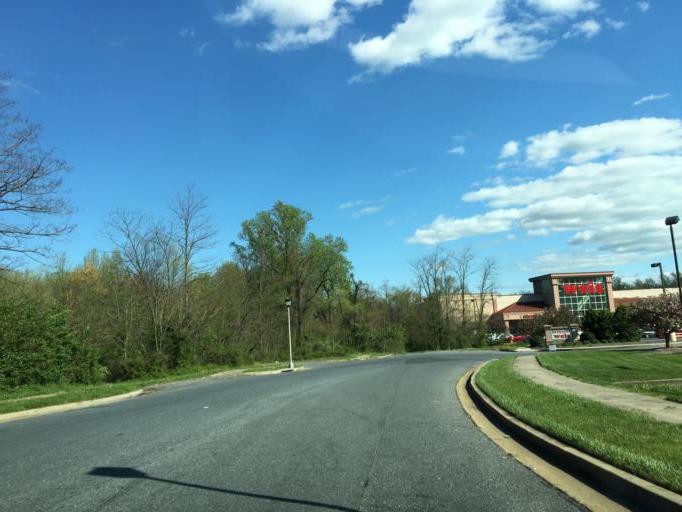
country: US
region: Maryland
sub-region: Frederick County
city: Thurmont
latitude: 39.6137
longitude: -77.4181
